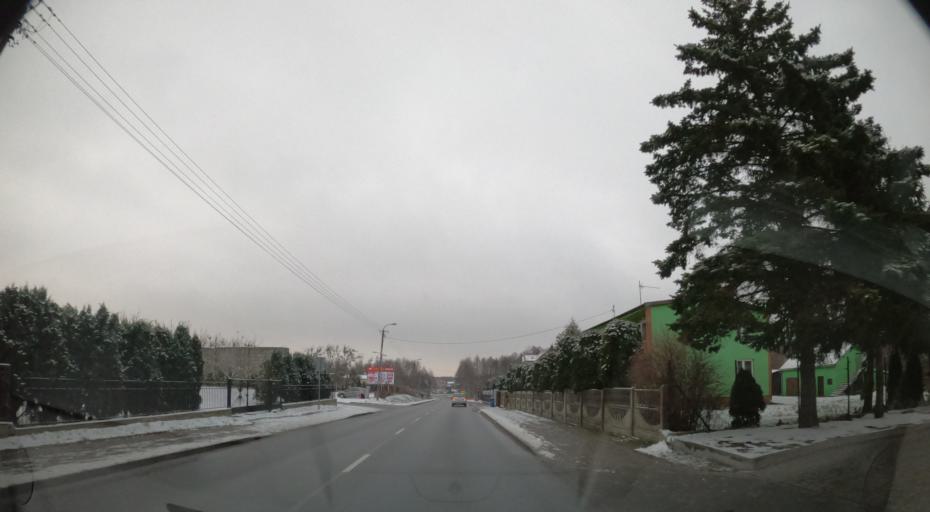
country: PL
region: Kujawsko-Pomorskie
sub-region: Powiat lipnowski
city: Wielgie
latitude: 52.7423
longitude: 19.2617
